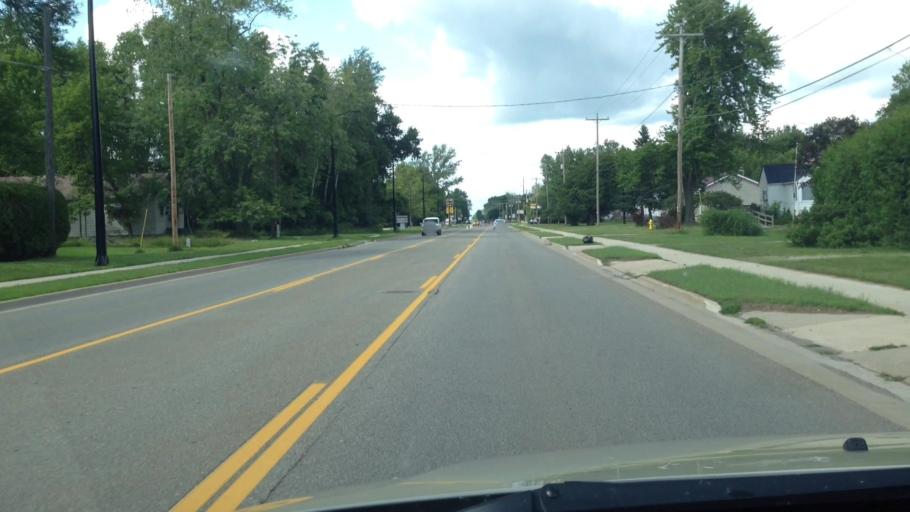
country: US
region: Michigan
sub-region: Menominee County
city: Menominee
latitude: 45.1407
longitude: -87.6121
